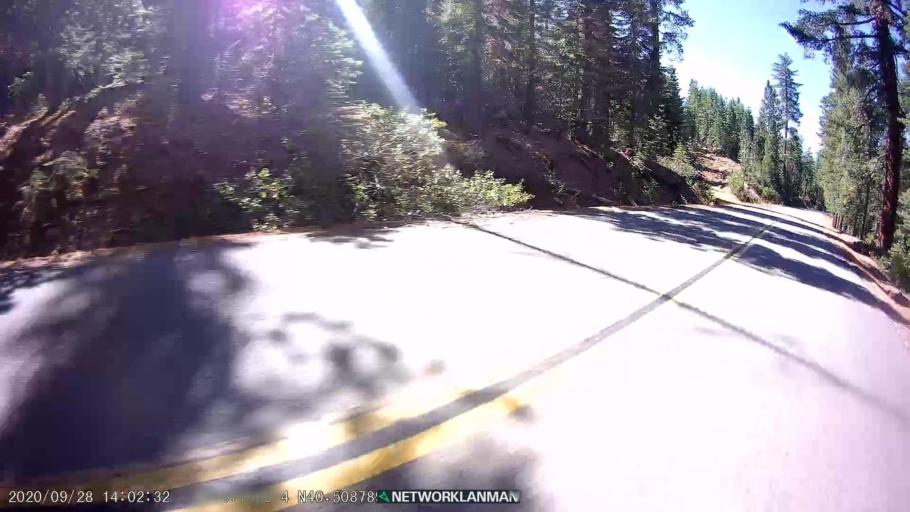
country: US
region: California
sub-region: Lassen County
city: Susanville
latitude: 40.5090
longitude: -120.7658
